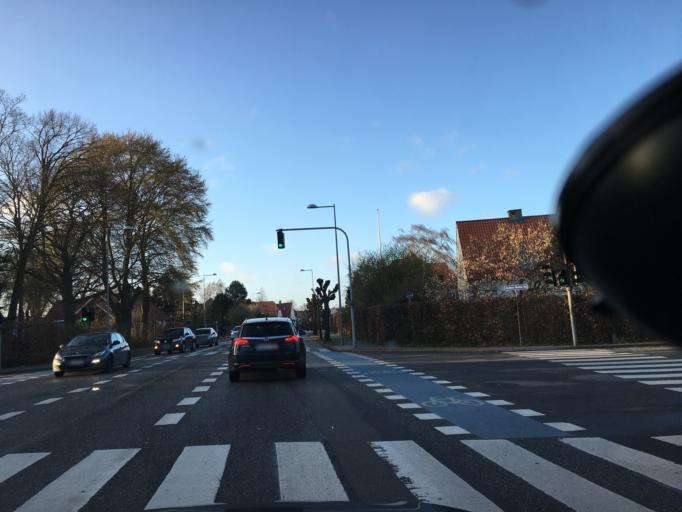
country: DK
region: North Denmark
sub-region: Alborg Kommune
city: Aalborg
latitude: 57.0473
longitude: 9.9033
